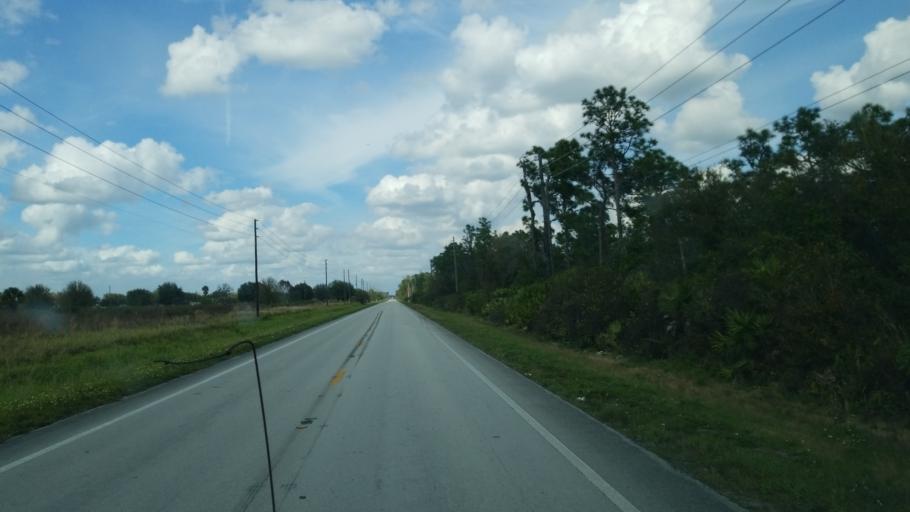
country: US
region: Florida
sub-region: Osceola County
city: Saint Cloud
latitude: 28.1126
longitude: -81.0763
